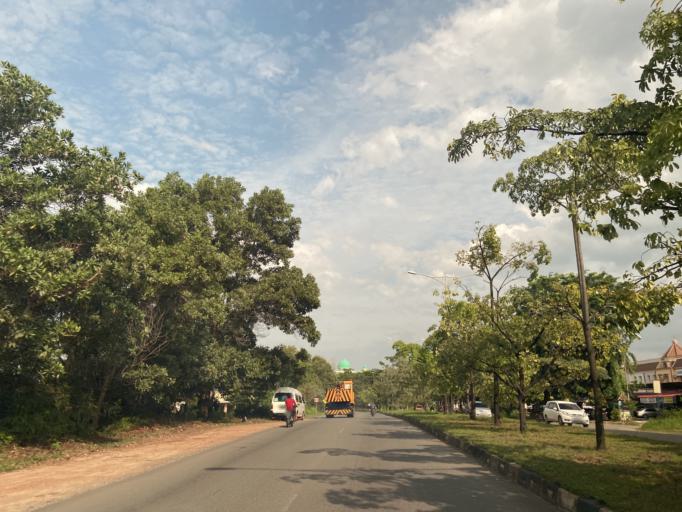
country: SG
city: Singapore
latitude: 1.1063
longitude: 104.0656
